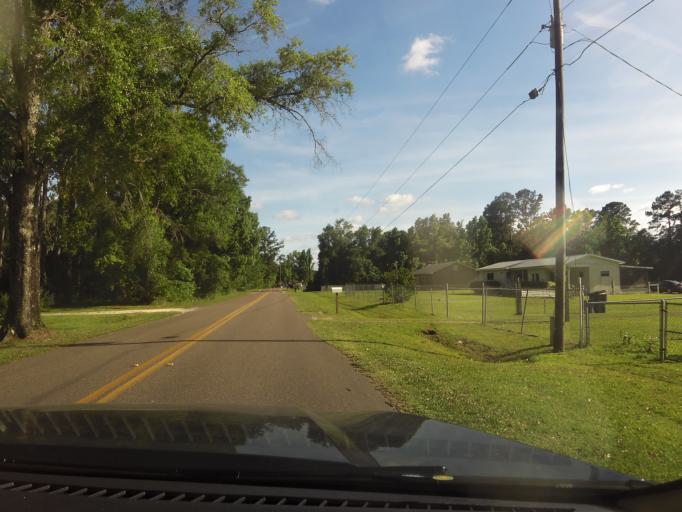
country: US
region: Florida
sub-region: Nassau County
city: Nassau Village-Ratliff
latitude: 30.5123
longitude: -81.7819
